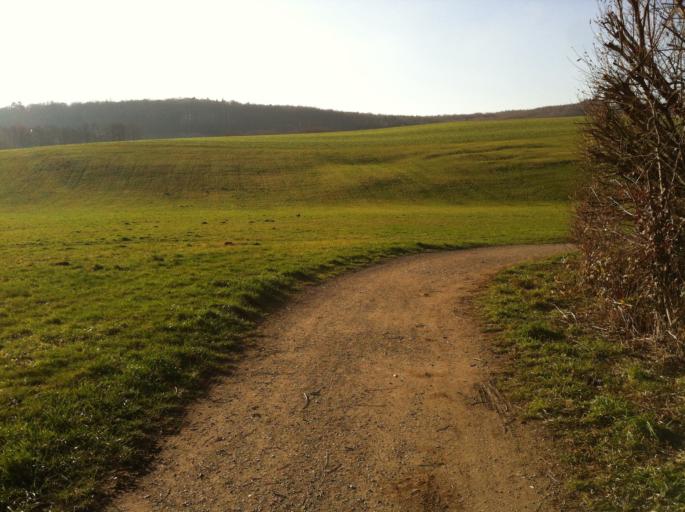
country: AT
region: Lower Austria
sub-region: Politischer Bezirk Wien-Umgebung
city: Gablitz
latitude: 48.2316
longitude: 16.1462
